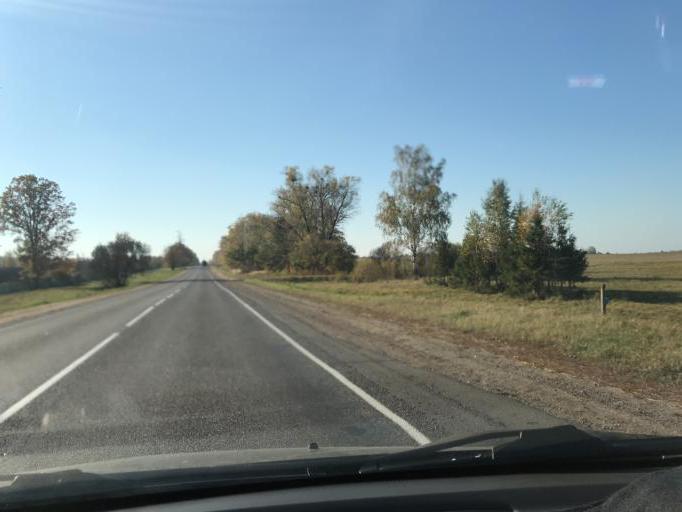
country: BY
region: Mogilev
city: Hlusha
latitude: 53.0926
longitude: 28.9342
